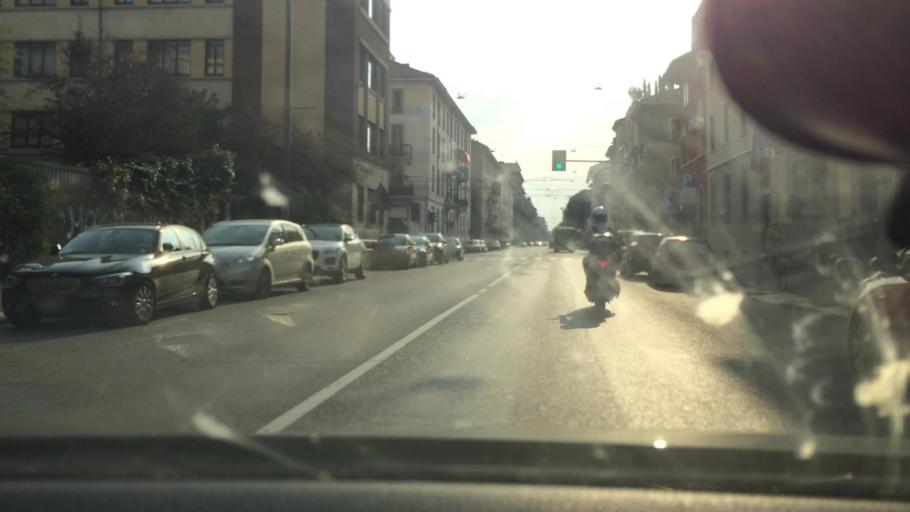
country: IT
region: Lombardy
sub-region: Citta metropolitana di Milano
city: Milano
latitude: 45.4860
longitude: 9.2202
